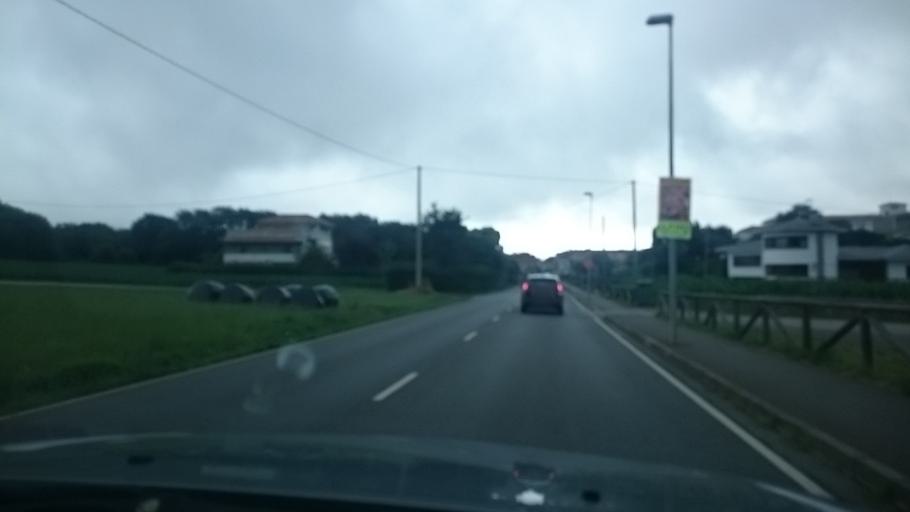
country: ES
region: Asturias
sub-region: Province of Asturias
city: Carrena
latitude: 43.4206
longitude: -4.8687
